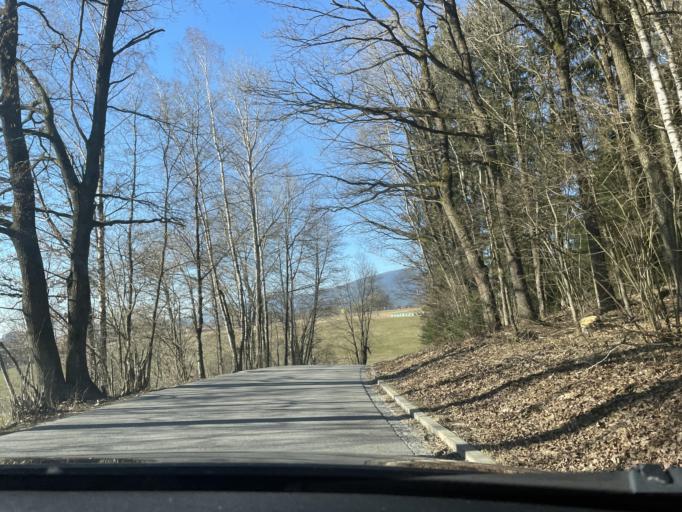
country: DE
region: Bavaria
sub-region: Lower Bavaria
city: Arnbruck
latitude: 49.1162
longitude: 13.0002
